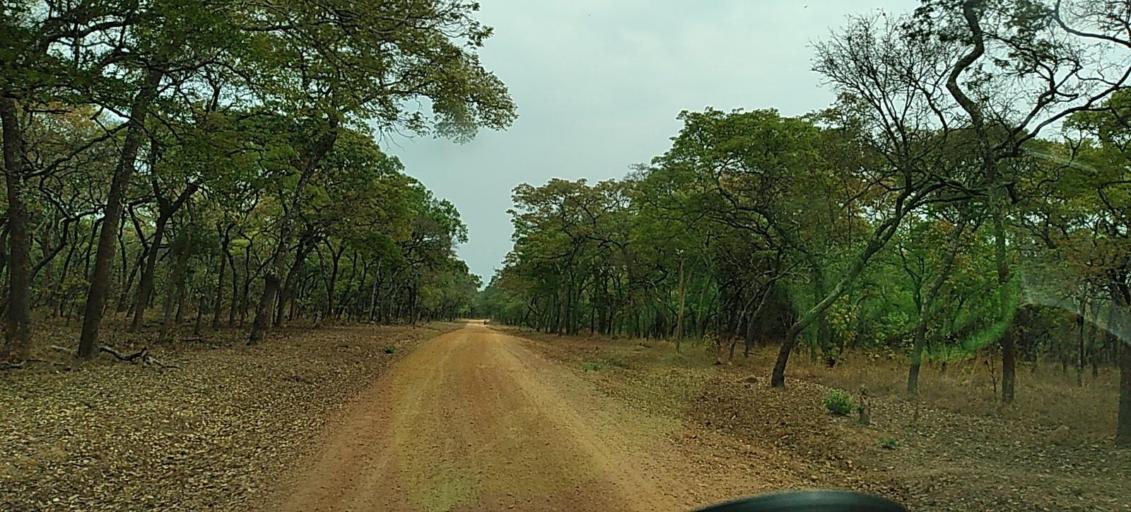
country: ZM
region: North-Western
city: Solwezi
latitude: -12.9253
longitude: 26.5613
